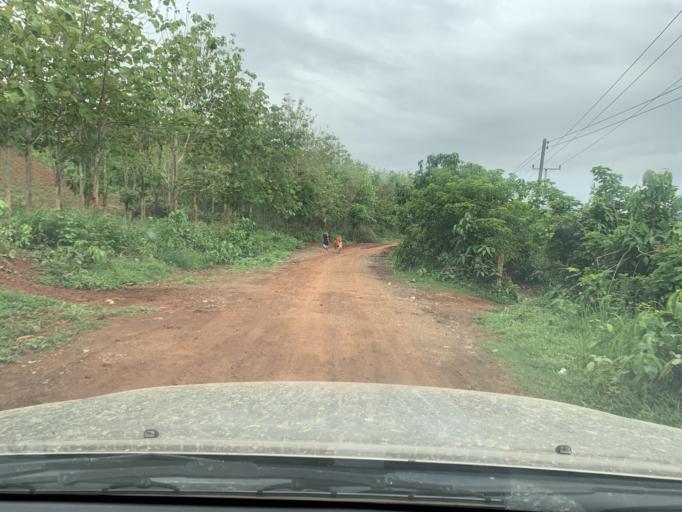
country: TH
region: Nan
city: Mae Charim
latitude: 18.4139
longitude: 101.4424
